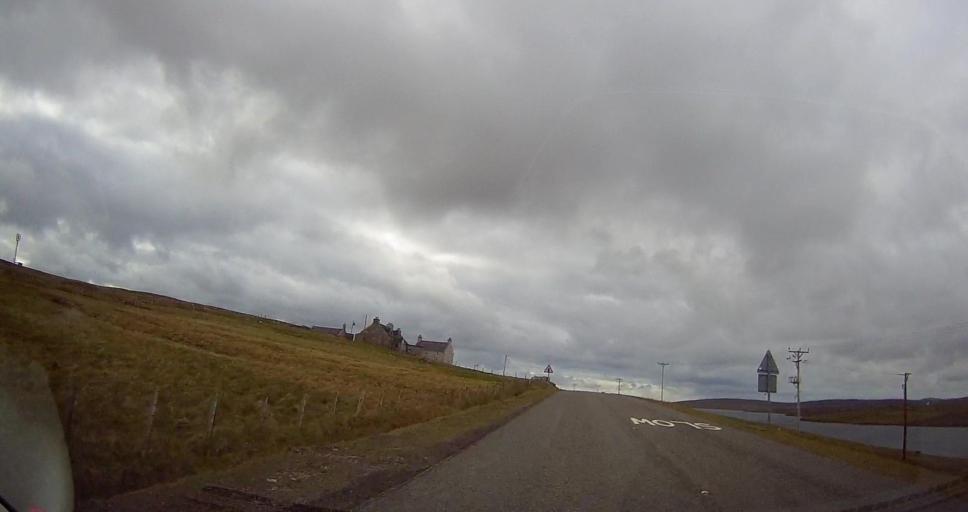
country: GB
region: Scotland
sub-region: Shetland Islands
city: Shetland
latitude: 60.6683
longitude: -1.0612
